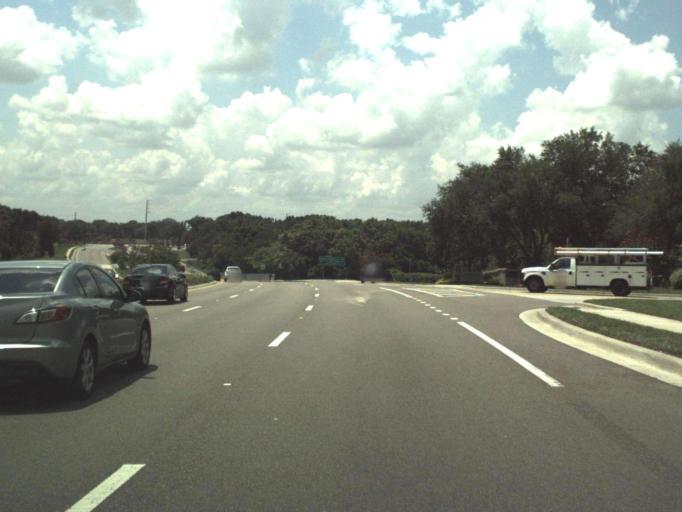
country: US
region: Florida
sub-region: Seminole County
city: Forest City
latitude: 28.6554
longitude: -81.4192
